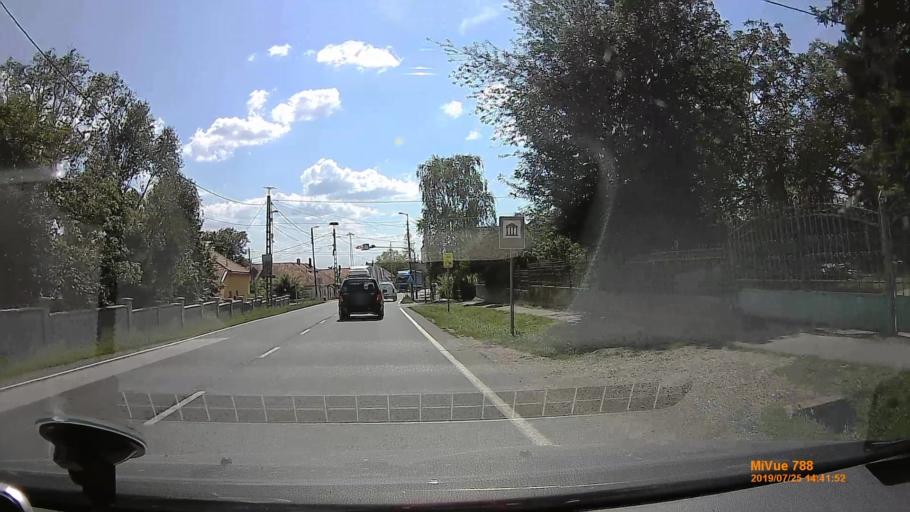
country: HU
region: Borsod-Abauj-Zemplen
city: Halmaj
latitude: 48.2810
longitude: 21.0265
